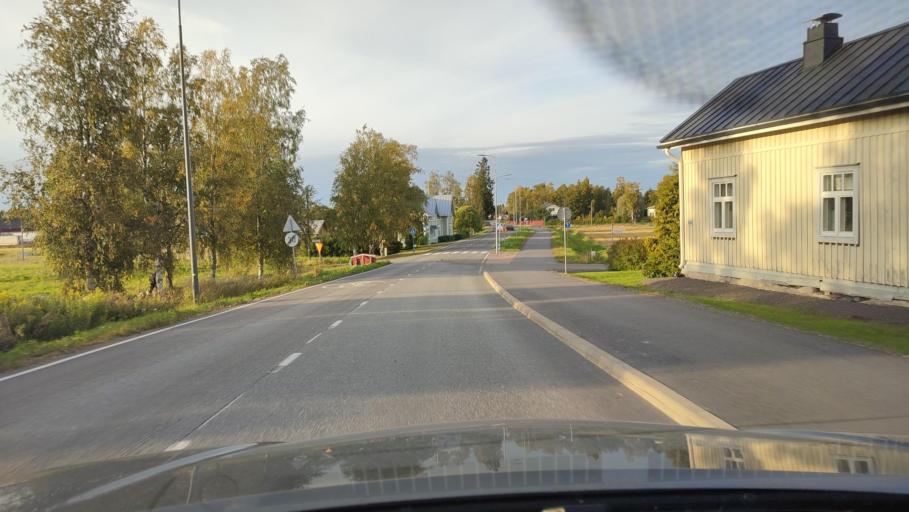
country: FI
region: Ostrobothnia
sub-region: Sydosterbotten
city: Kristinestad
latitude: 62.2484
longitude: 21.5210
